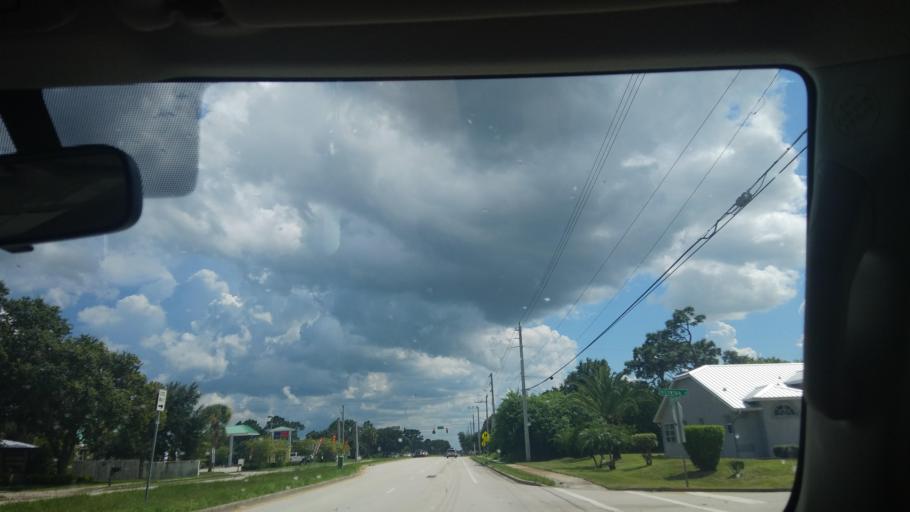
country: US
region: Florida
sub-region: Brevard County
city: Palm Bay
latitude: 27.9887
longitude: -80.6486
